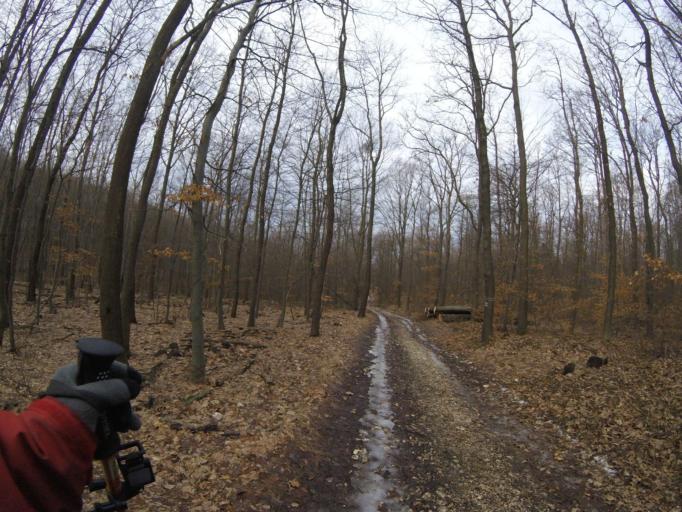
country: HU
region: Komarom-Esztergom
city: Kesztolc
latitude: 47.7217
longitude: 18.8245
